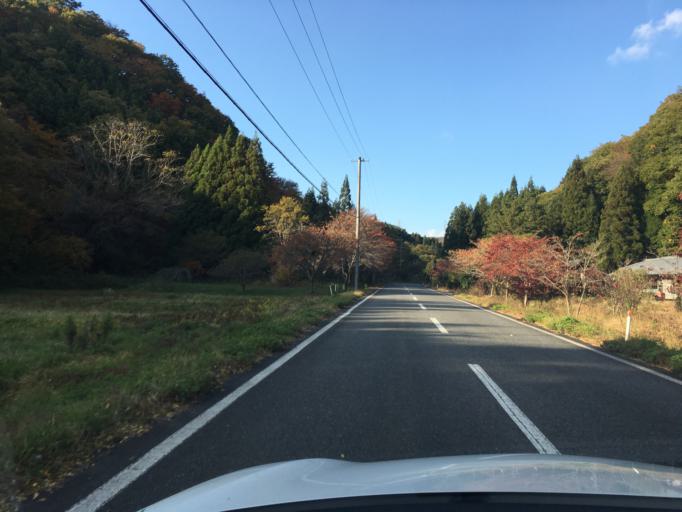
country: JP
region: Fukushima
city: Iwaki
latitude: 37.2429
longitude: 140.7625
